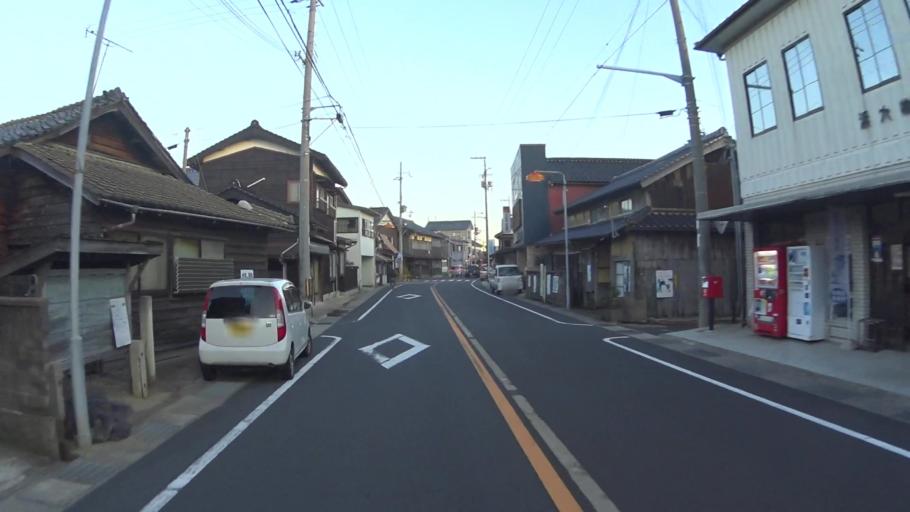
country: JP
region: Kyoto
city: Miyazu
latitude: 35.6876
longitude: 135.0216
